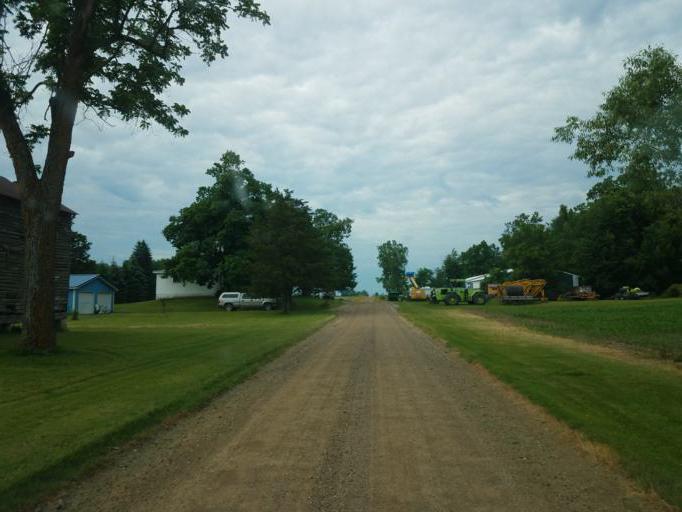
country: US
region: Michigan
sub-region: Barry County
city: Nashville
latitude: 42.6350
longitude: -84.9953
